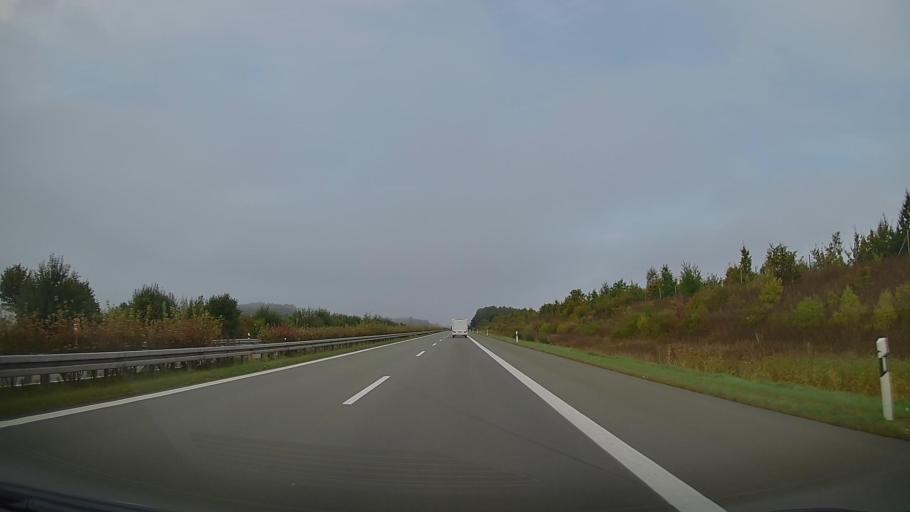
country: DE
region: Mecklenburg-Vorpommern
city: Franzburg
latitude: 54.0784
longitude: 12.8643
